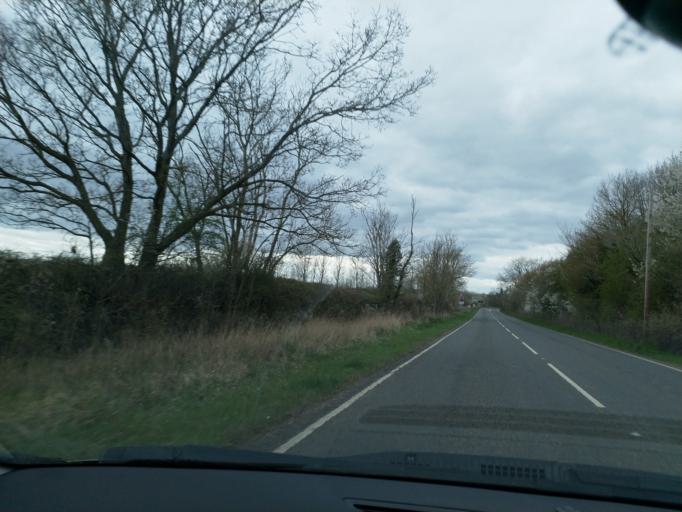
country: GB
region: England
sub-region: Warwickshire
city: Harbury
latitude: 52.1460
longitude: -1.4656
